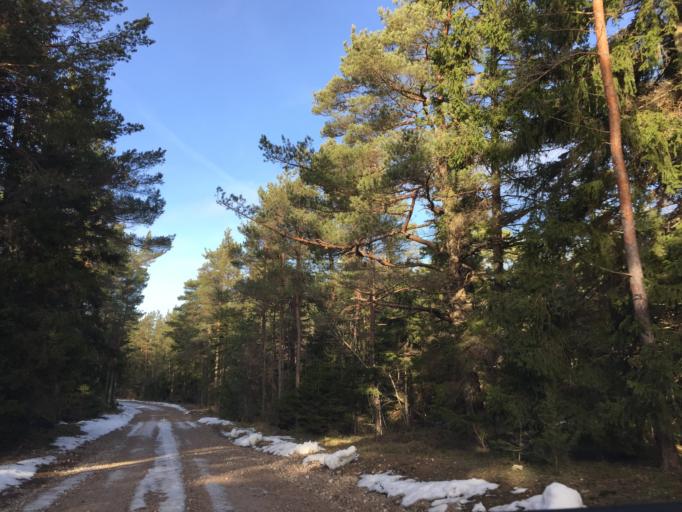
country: EE
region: Saare
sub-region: Kuressaare linn
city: Kuressaare
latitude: 58.4758
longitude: 21.9545
